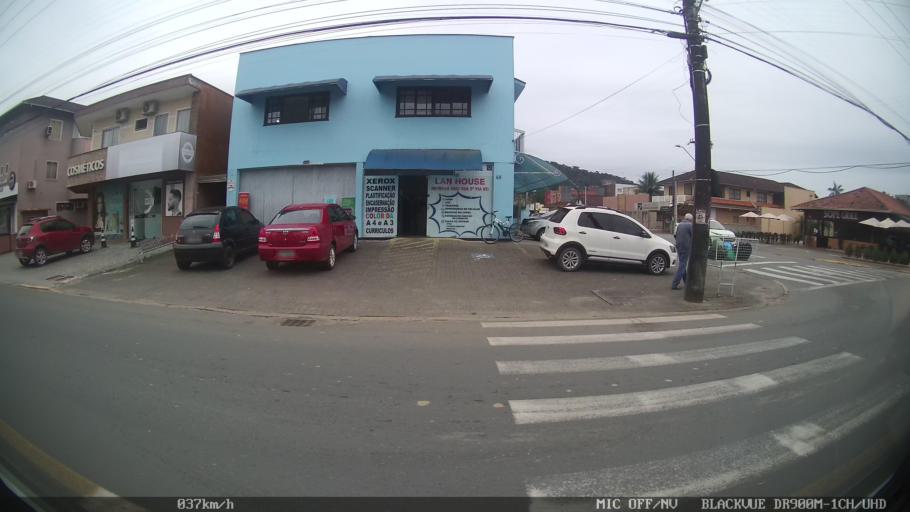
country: BR
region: Santa Catarina
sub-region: Joinville
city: Joinville
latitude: -26.2088
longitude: -48.9072
